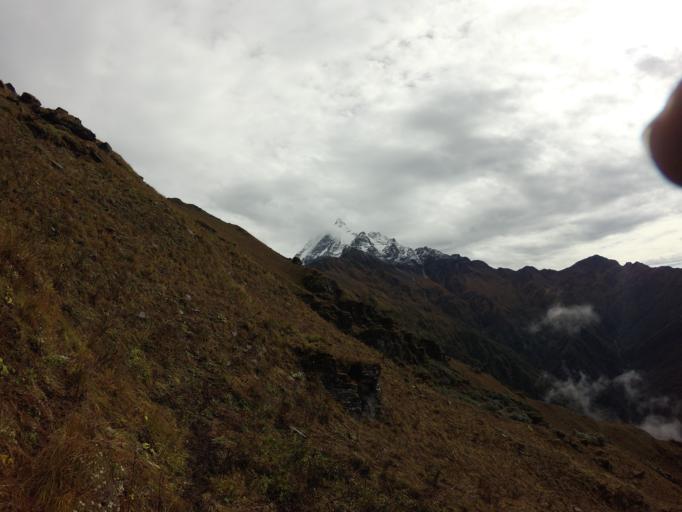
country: NP
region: Western Region
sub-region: Dhawalagiri Zone
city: Chitre
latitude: 28.4463
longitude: 83.8768
